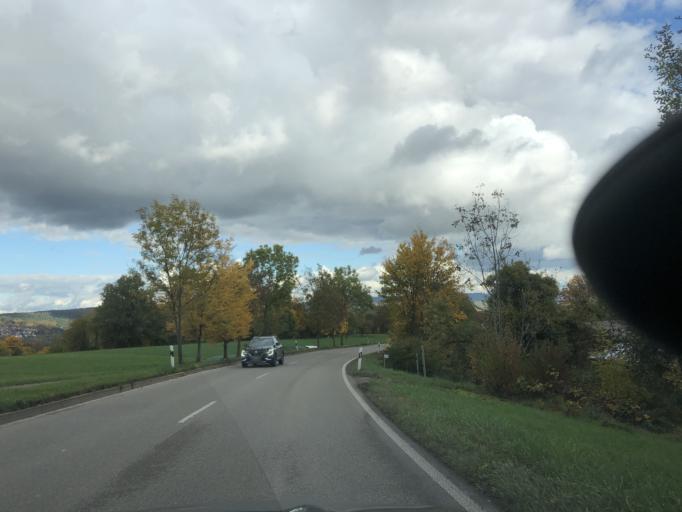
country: DE
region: Baden-Wuerttemberg
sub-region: Regierungsbezirk Stuttgart
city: Winterbach
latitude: 48.7866
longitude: 9.4617
